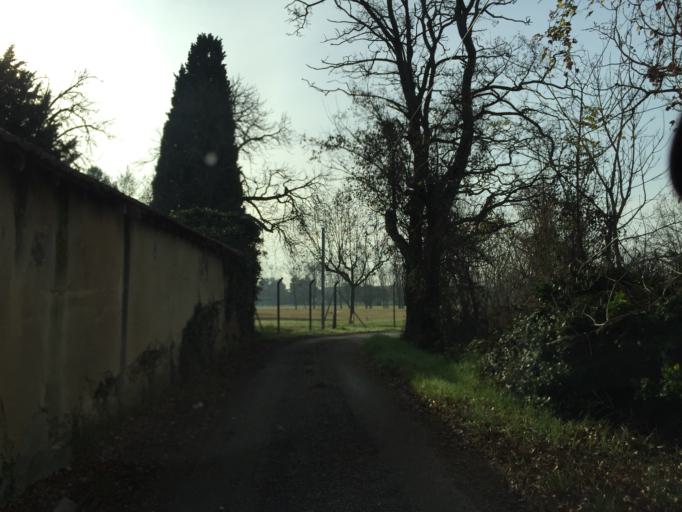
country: FR
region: Provence-Alpes-Cote d'Azur
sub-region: Departement du Vaucluse
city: Camaret-sur-Aigues
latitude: 44.1461
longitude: 4.8546
